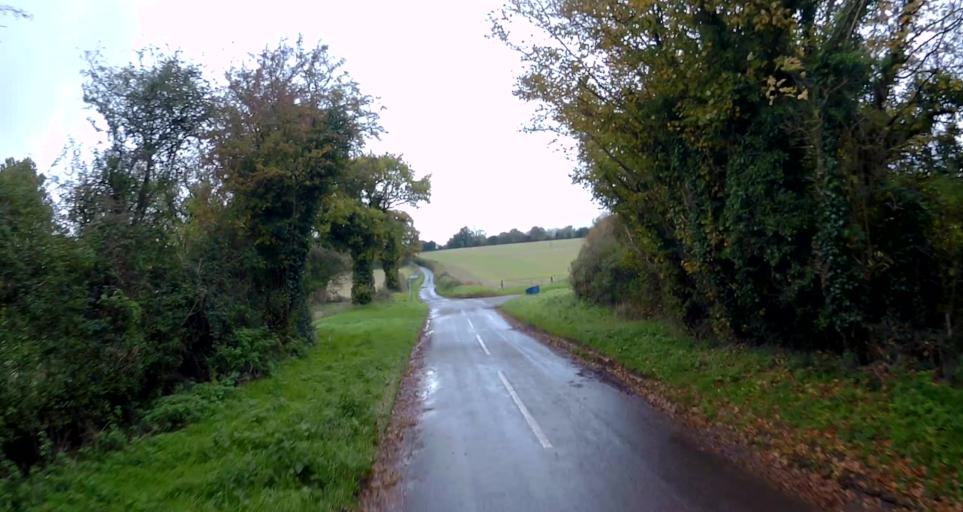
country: GB
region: England
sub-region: Hampshire
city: Four Marks
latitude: 51.1532
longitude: -1.0840
